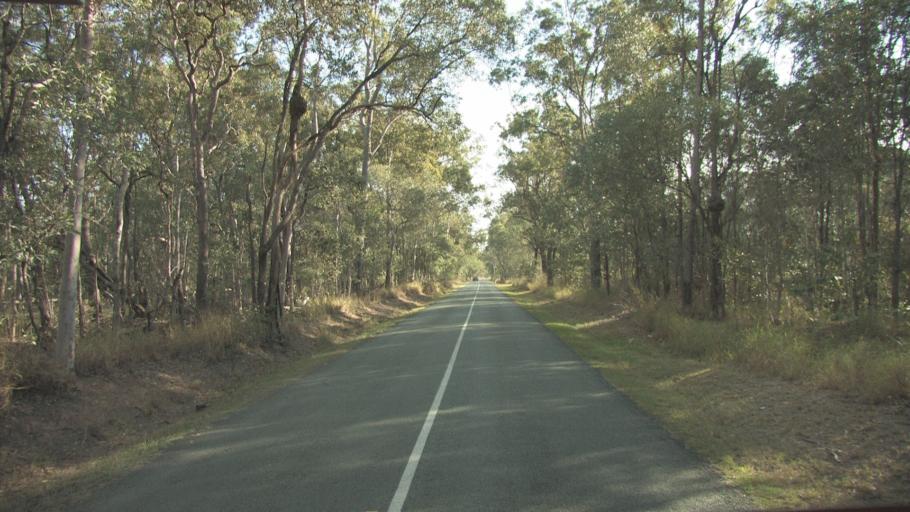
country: AU
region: Queensland
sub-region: Logan
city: Cedar Vale
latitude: -27.8514
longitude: 153.1305
